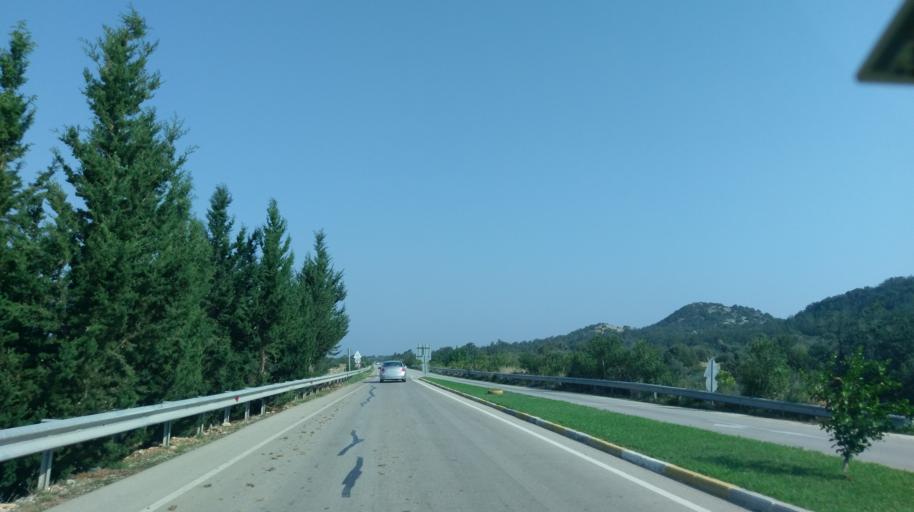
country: CY
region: Ammochostos
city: Lefkonoiko
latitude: 35.3731
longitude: 33.7121
